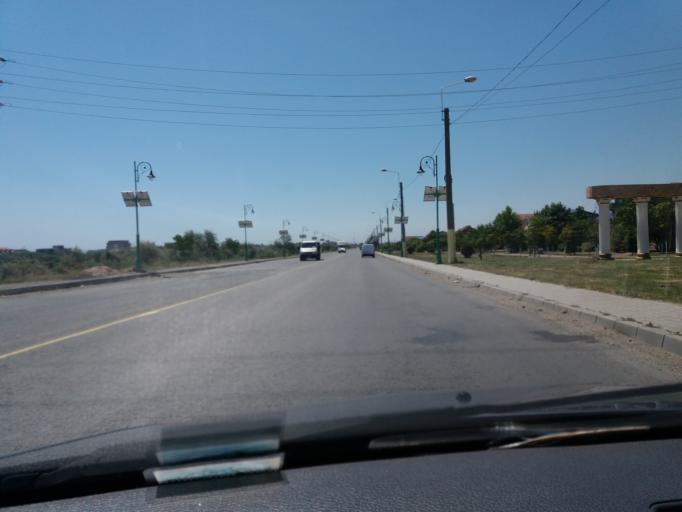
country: RO
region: Constanta
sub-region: Comuna Navodari
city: Navodari
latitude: 44.3148
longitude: 28.6167
